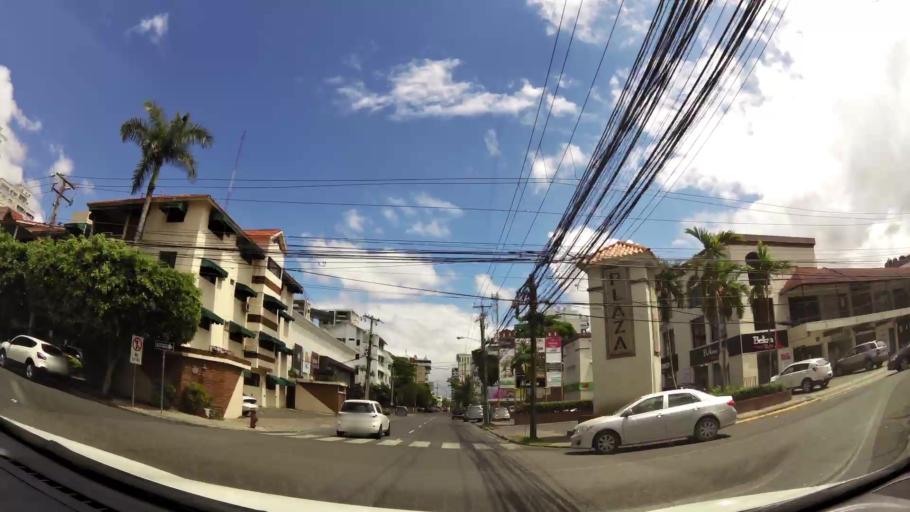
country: DO
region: Nacional
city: La Julia
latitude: 18.4724
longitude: -69.9405
